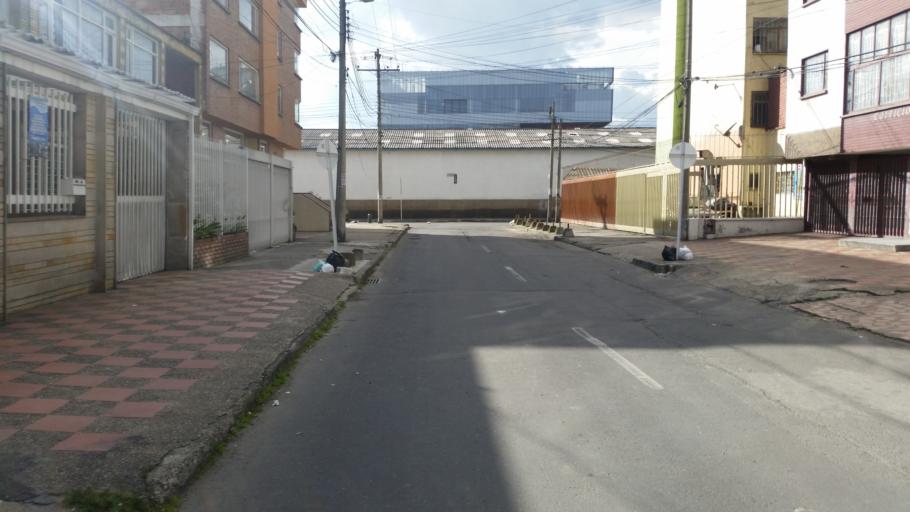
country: CO
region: Bogota D.C.
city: Bogota
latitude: 4.6272
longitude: -74.0914
